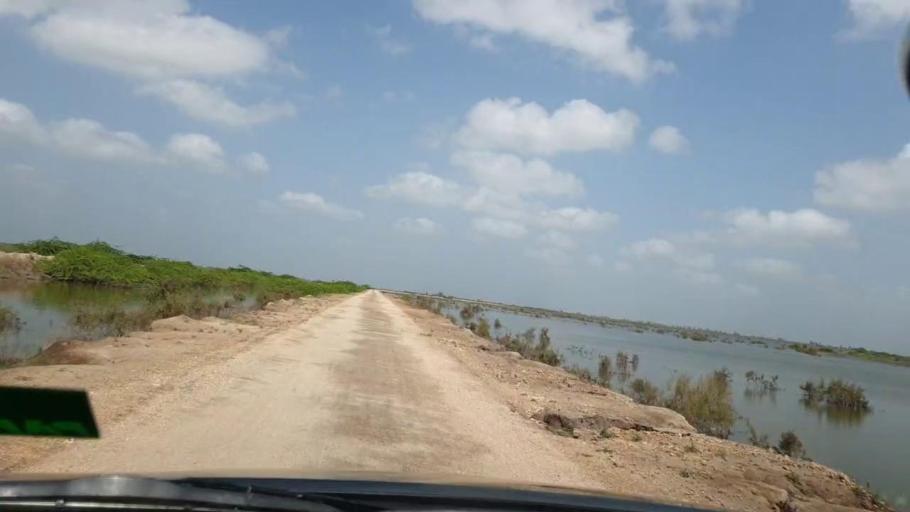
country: PK
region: Sindh
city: Kadhan
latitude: 24.5782
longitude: 69.1425
